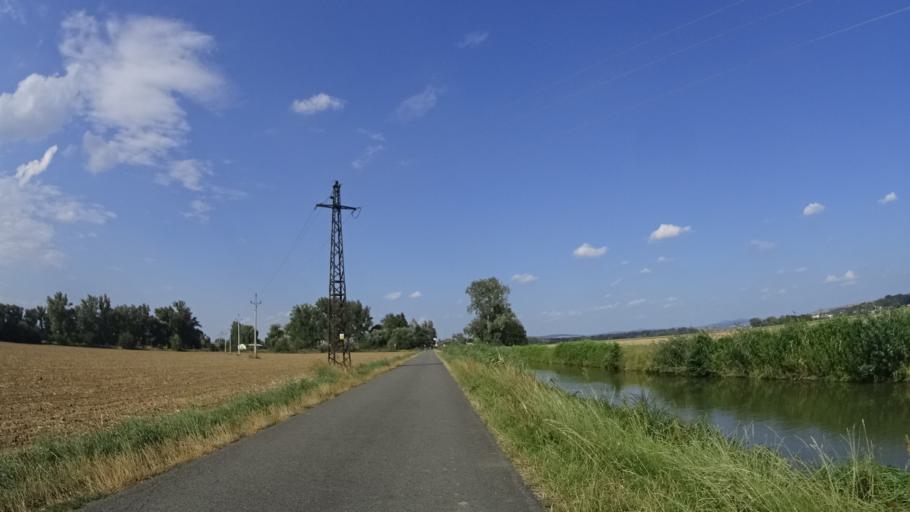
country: CZ
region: Zlin
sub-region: Okres Uherske Hradiste
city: Uherske Hradiste
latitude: 49.0825
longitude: 17.4642
